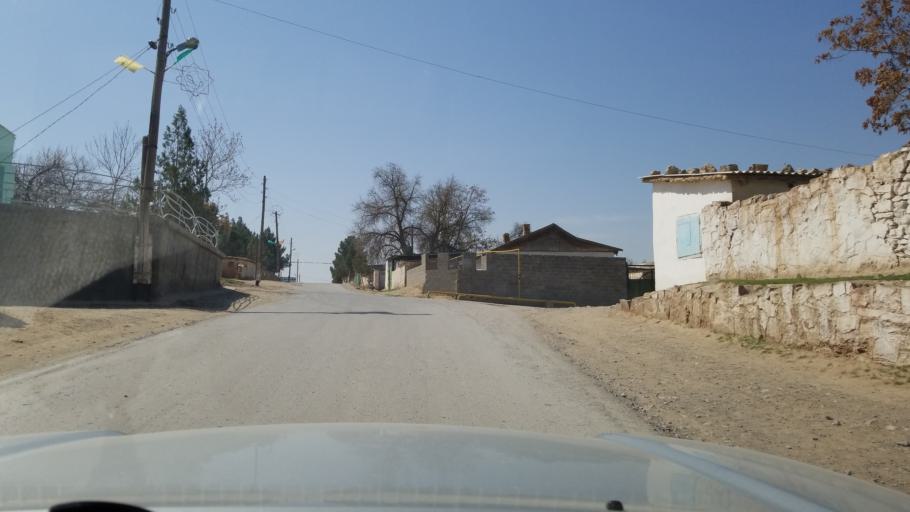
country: TM
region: Lebap
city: Gowurdak
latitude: 37.8701
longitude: 66.4453
